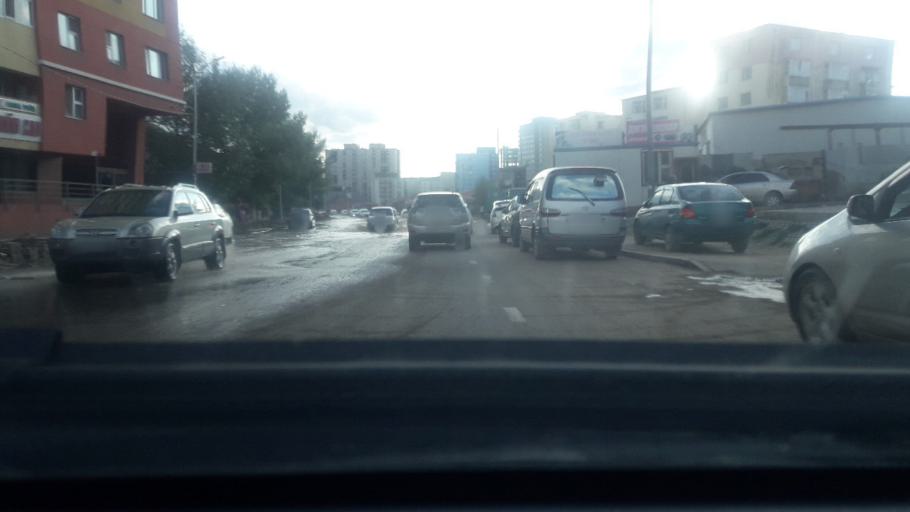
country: MN
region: Ulaanbaatar
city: Ulaanbaatar
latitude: 47.9185
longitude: 106.9821
